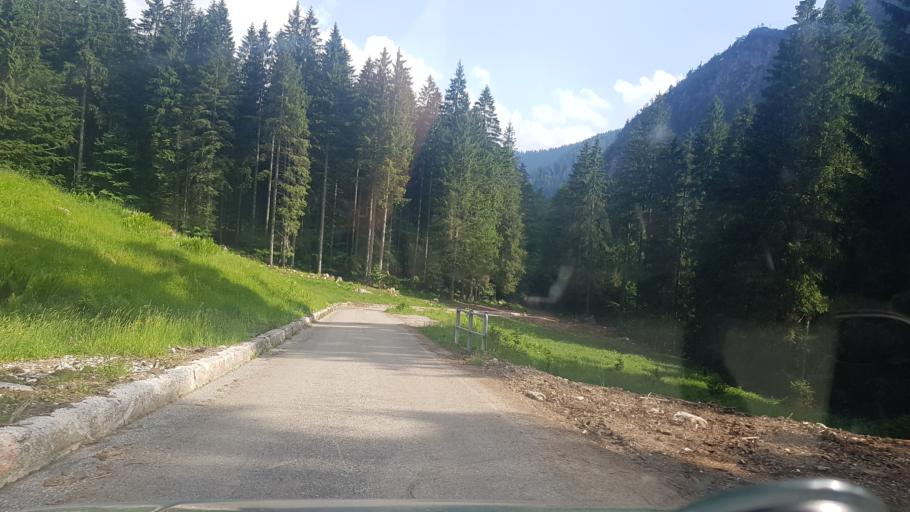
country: IT
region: Friuli Venezia Giulia
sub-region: Provincia di Udine
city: Paularo
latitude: 46.5394
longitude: 13.2054
